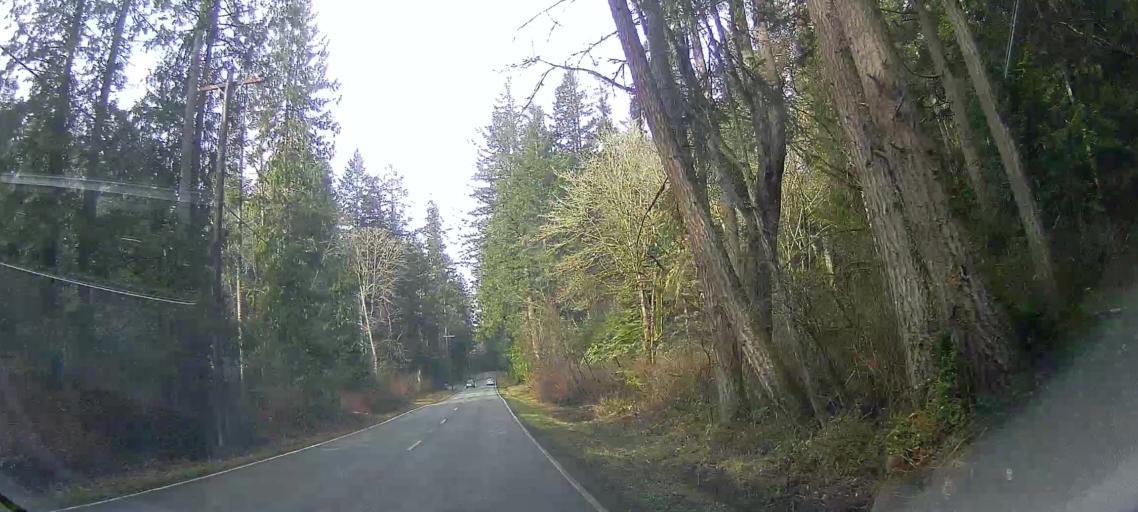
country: US
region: Washington
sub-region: Island County
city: Camano
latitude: 48.1440
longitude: -122.5079
